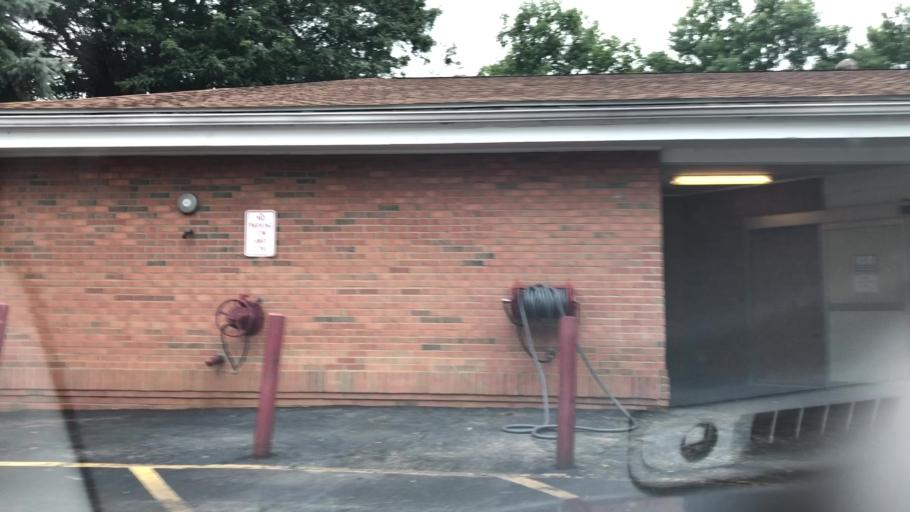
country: US
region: Ohio
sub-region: Summit County
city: Montrose-Ghent
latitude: 41.1316
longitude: -81.6407
